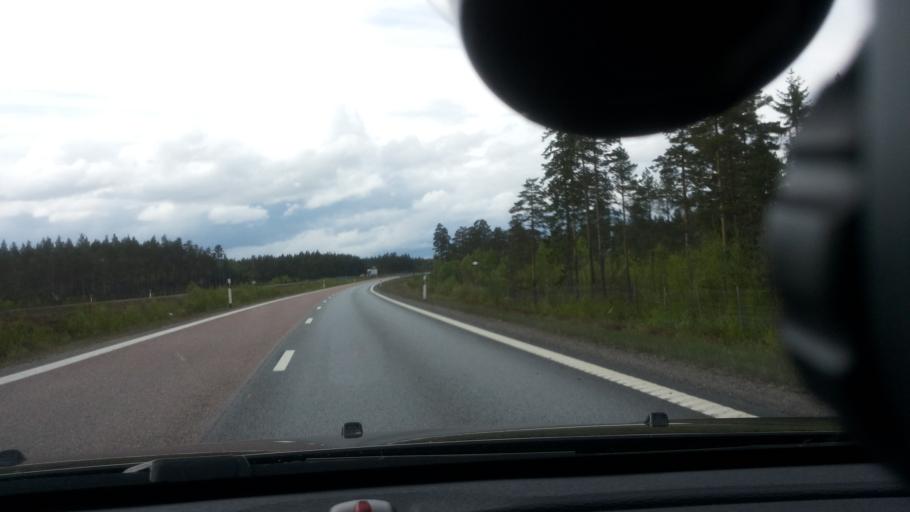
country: SE
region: Gaevleborg
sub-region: Soderhamns Kommun
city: Soderhamn
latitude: 61.3766
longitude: 16.9970
